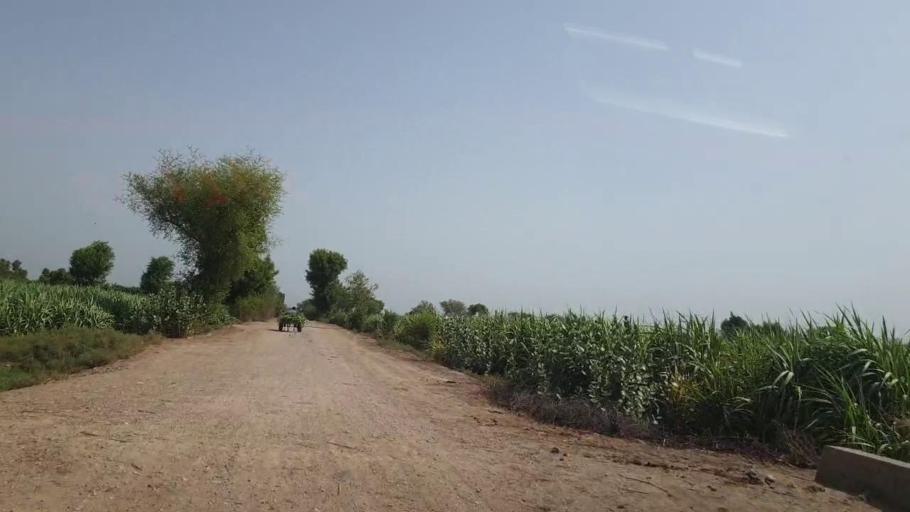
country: PK
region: Sindh
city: Daur
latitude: 26.3149
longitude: 68.2154
